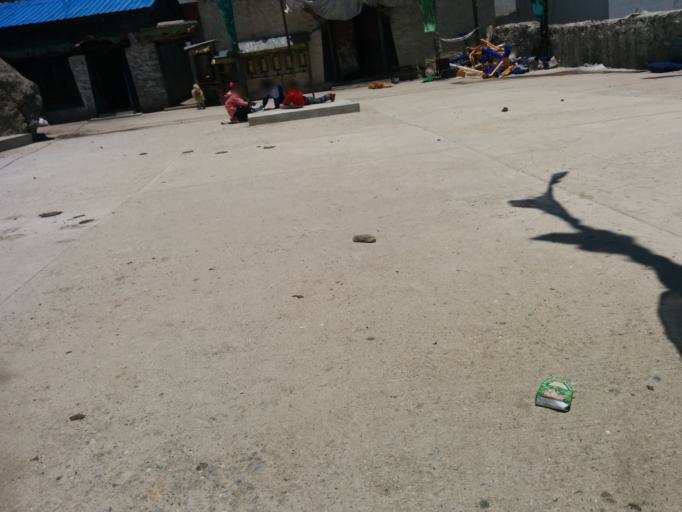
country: CN
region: Tibet Autonomous Region
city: Chongdui
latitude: 28.1609
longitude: 85.9774
